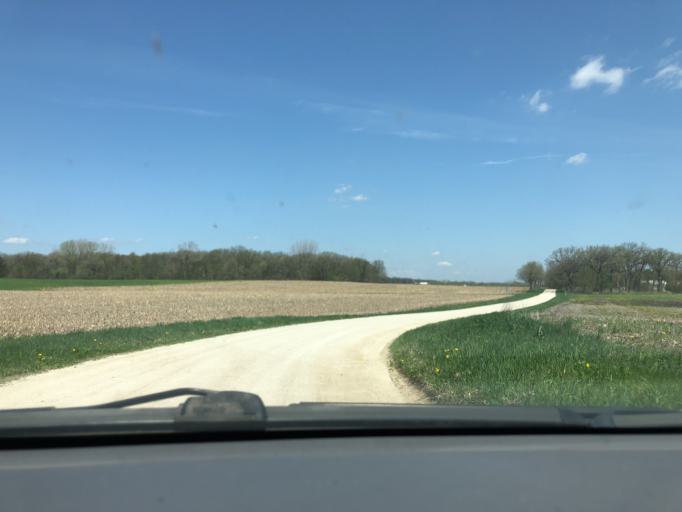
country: US
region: Illinois
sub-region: Kane County
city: Pingree Grove
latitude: 42.0741
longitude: -88.4666
